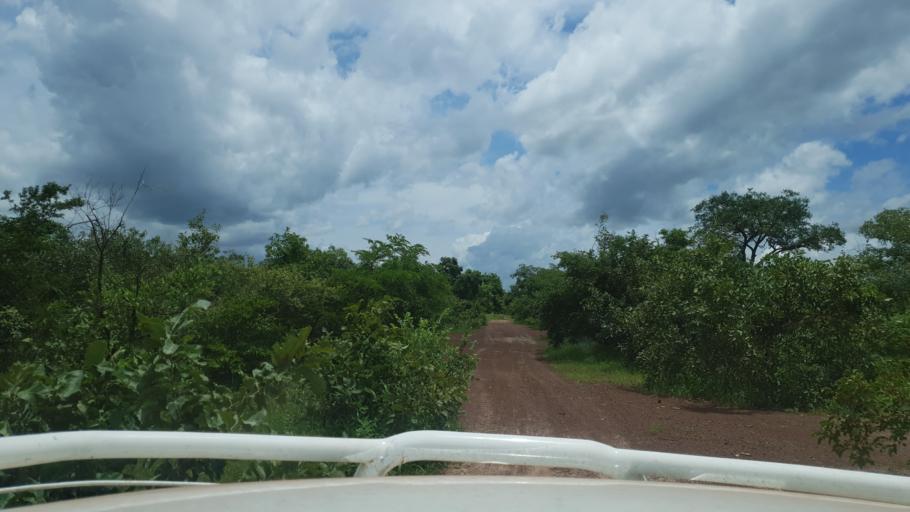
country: ML
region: Koulikoro
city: Banamba
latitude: 13.1944
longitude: -7.3211
